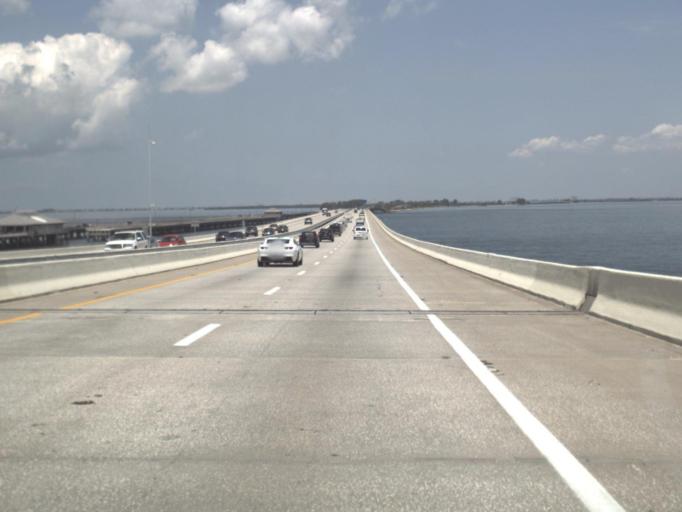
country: US
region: Florida
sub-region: Pinellas County
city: Tierra Verde
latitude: 27.6305
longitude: -82.6628
